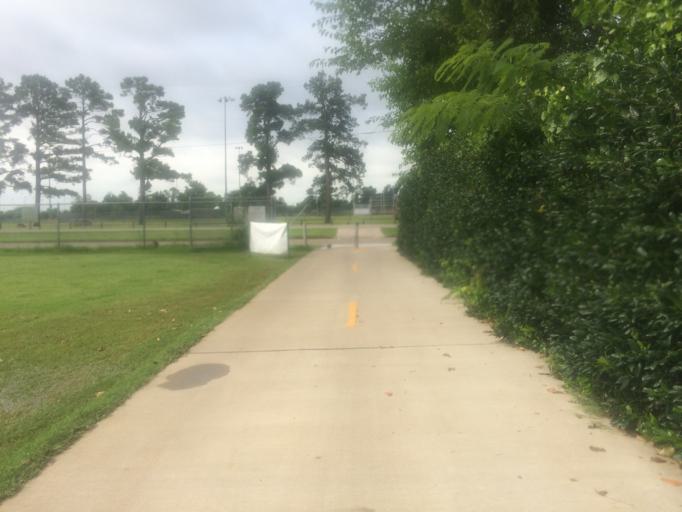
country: US
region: Oklahoma
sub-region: Cleveland County
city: Norman
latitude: 35.1972
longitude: -97.4401
